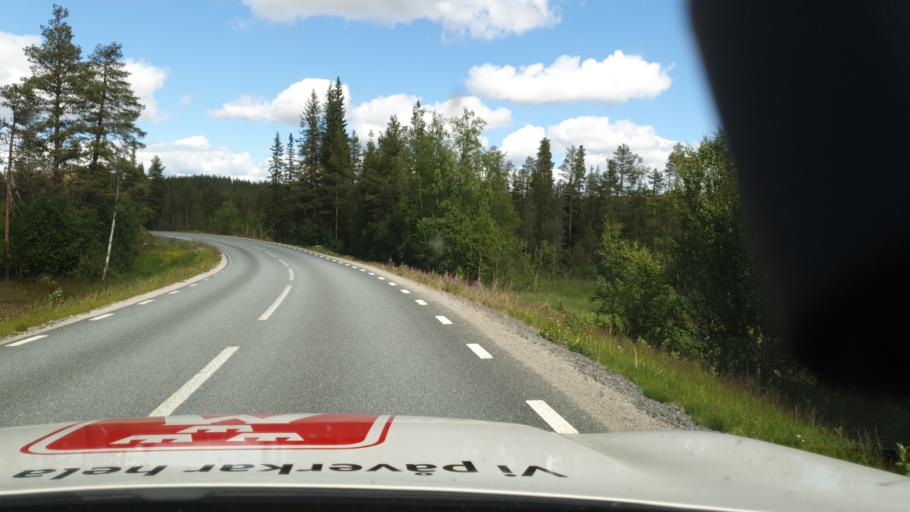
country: SE
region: Vaesterbotten
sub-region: Sorsele Kommun
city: Sorsele
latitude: 65.4670
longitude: 17.5710
